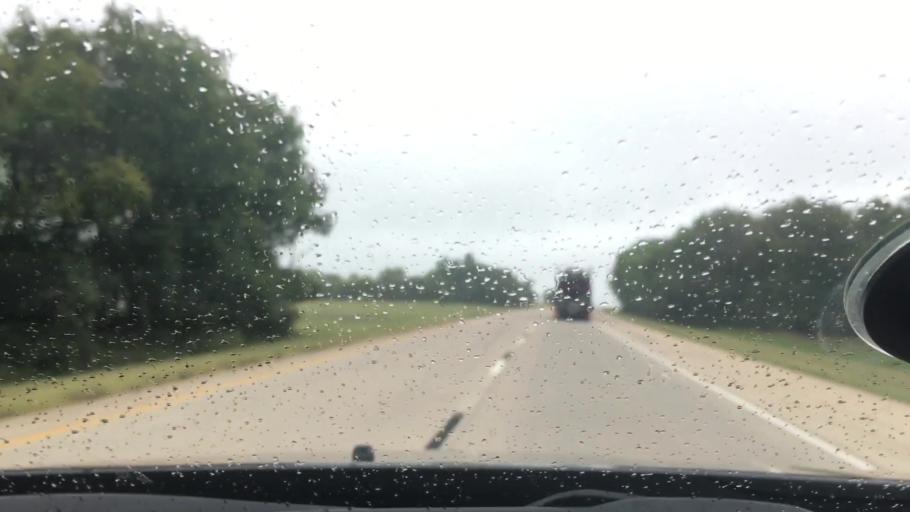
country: US
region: Oklahoma
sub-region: Okmulgee County
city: Henryetta
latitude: 35.4327
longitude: -95.9355
